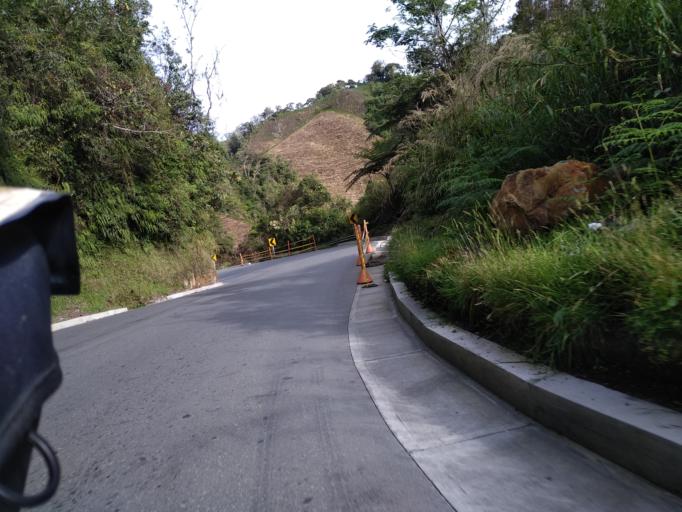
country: CO
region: Tolima
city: Herveo
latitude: 5.1372
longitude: -75.1842
